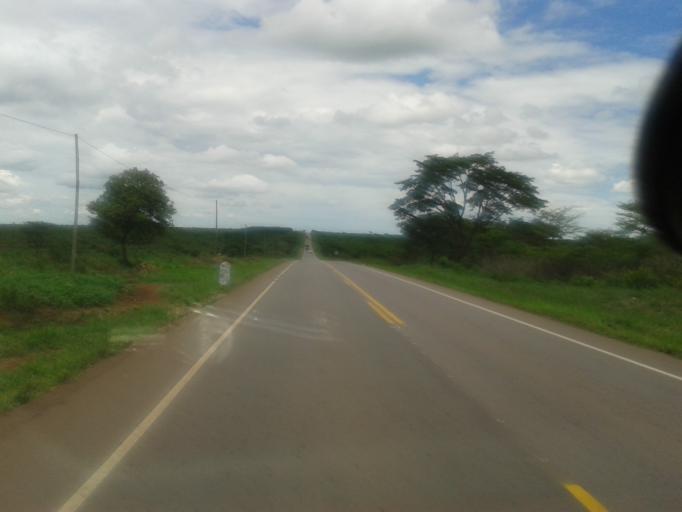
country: UG
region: Western Region
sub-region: Kiryandongo District
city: Masindi Port
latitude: 1.7633
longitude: 32.0202
